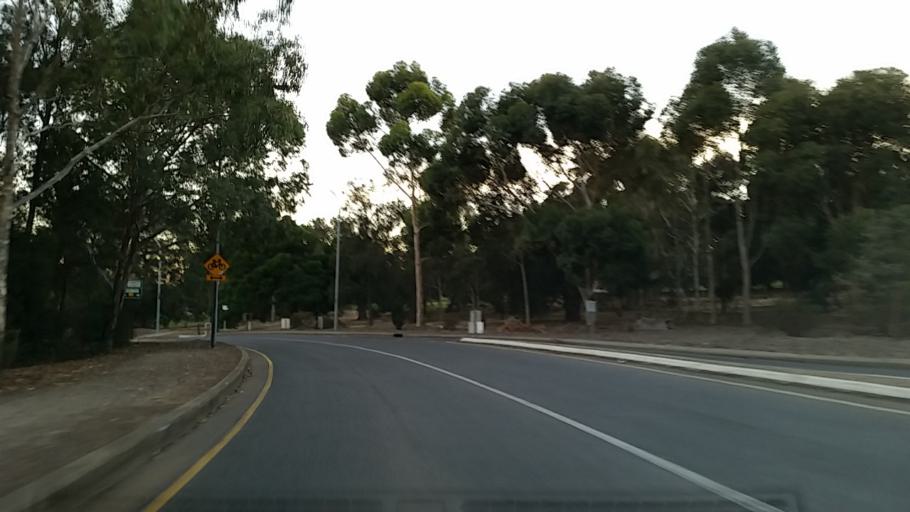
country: AU
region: South Australia
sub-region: Adelaide
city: North Adelaide
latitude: -34.9040
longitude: 138.5845
